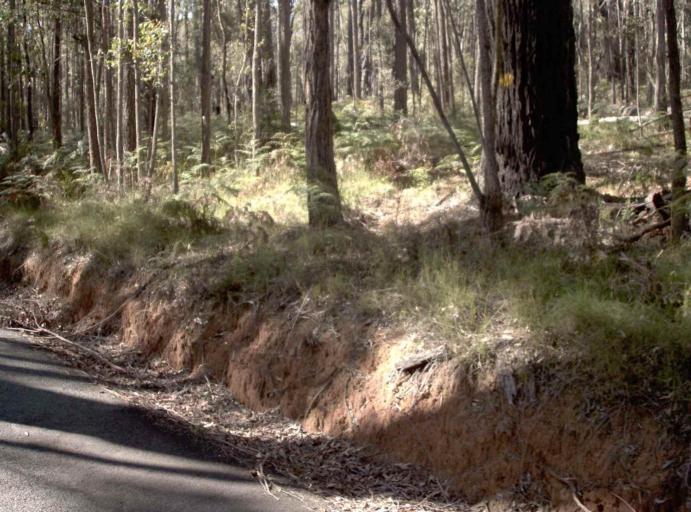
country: AU
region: New South Wales
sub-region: Bombala
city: Bombala
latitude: -37.3850
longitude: 148.6204
